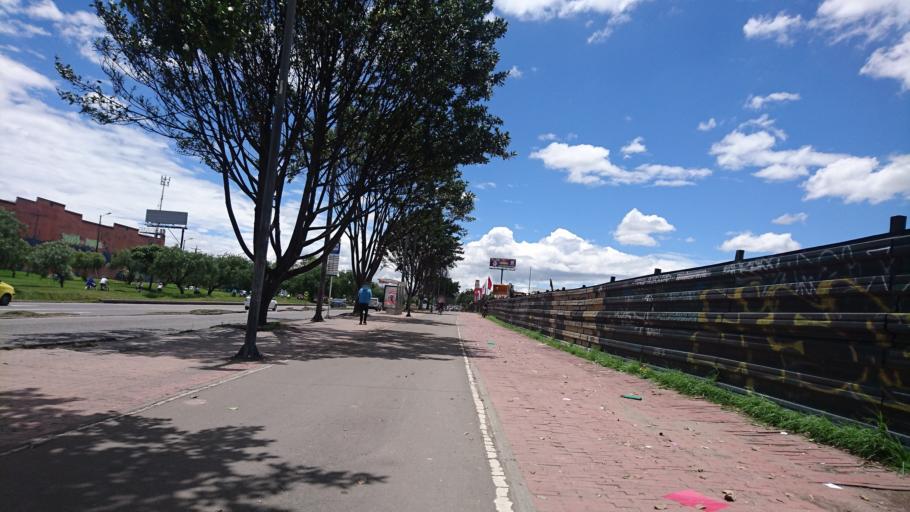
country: CO
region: Bogota D.C.
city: Bogota
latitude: 4.6559
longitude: -74.1212
